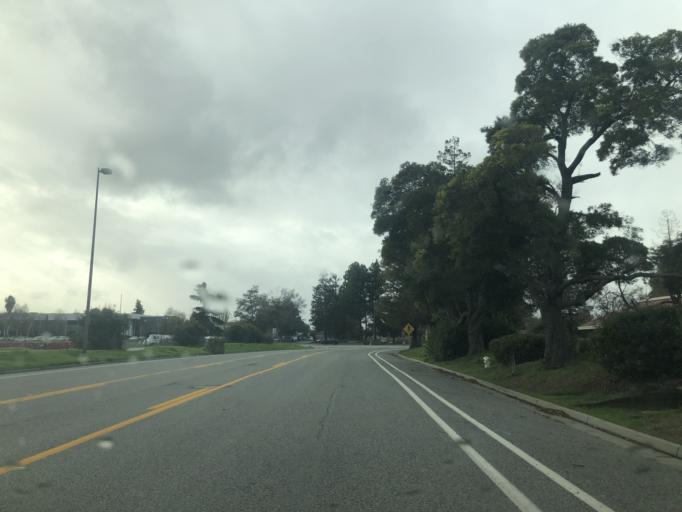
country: US
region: California
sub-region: Santa Clara County
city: Santa Clara
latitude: 37.4022
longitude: -121.9833
